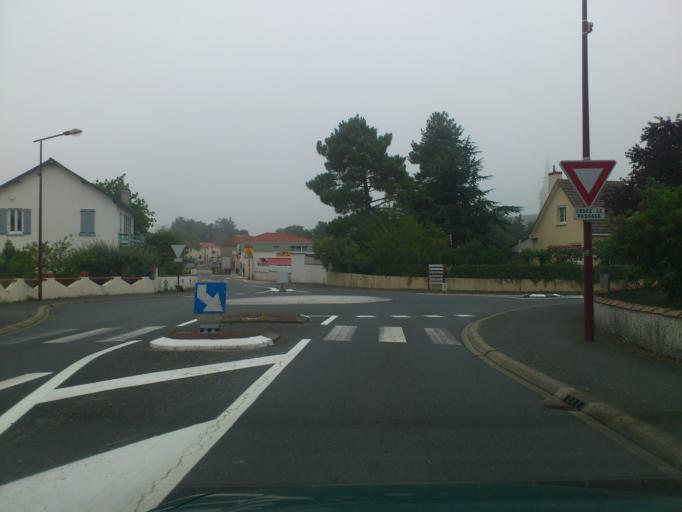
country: FR
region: Pays de la Loire
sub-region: Departement de la Loire-Atlantique
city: Saint-Hilaire-de-Clisson
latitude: 47.0603
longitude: -1.3097
